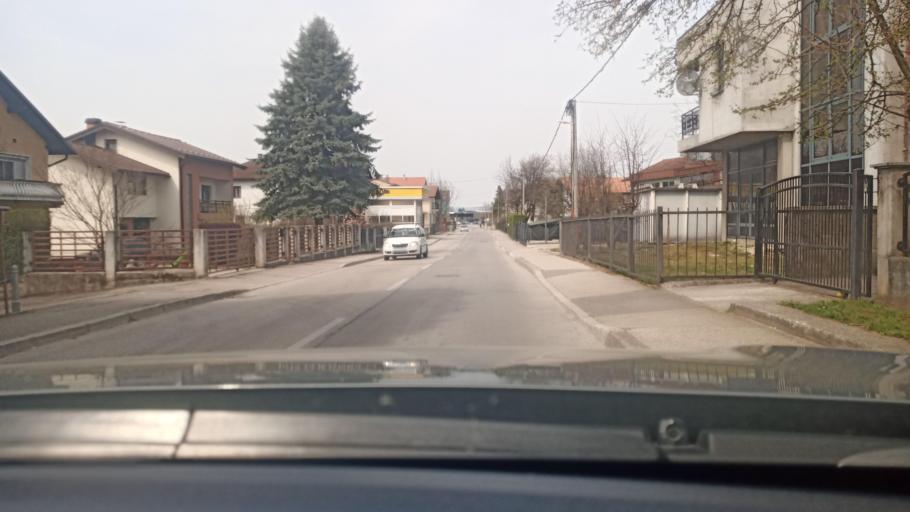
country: BA
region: Federation of Bosnia and Herzegovina
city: Bihac
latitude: 44.8203
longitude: 15.8664
